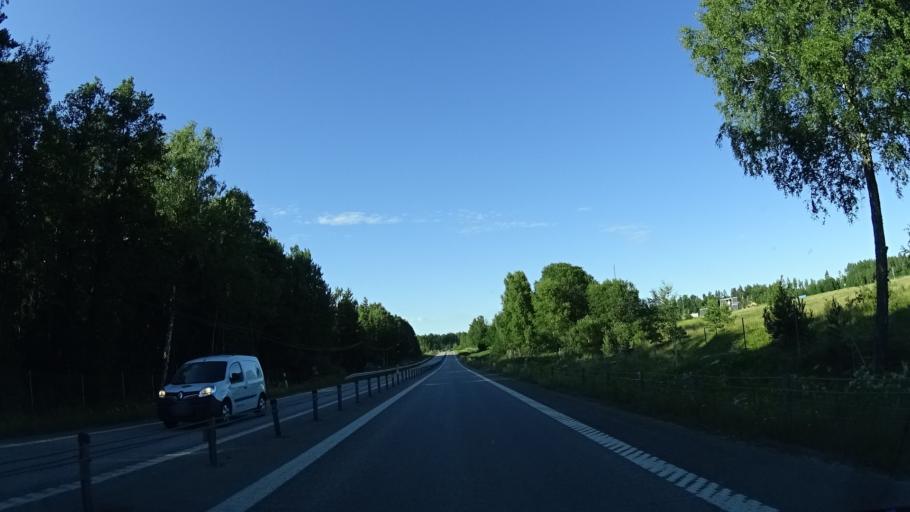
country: SE
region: Stockholm
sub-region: Vallentuna Kommun
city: Vallentuna
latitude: 59.5040
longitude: 18.1703
